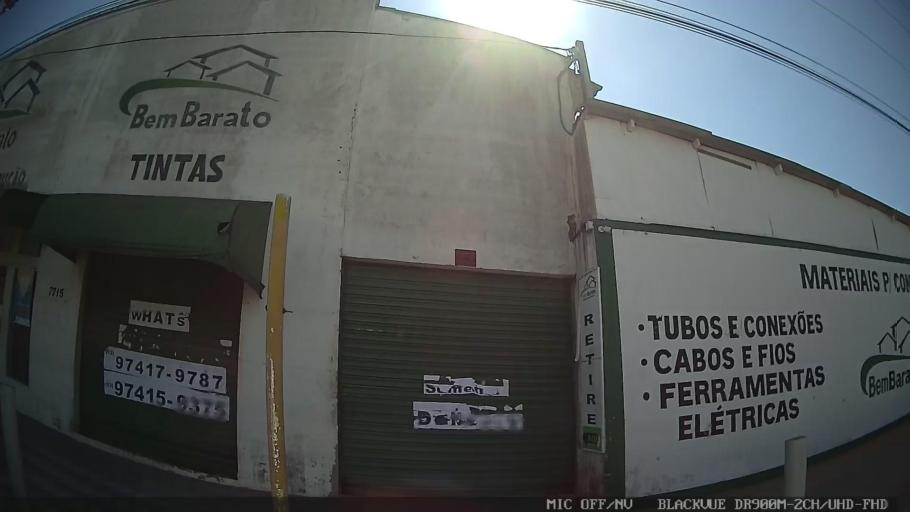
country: BR
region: Sao Paulo
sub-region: Itanhaem
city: Itanhaem
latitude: -24.1479
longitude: -46.7281
